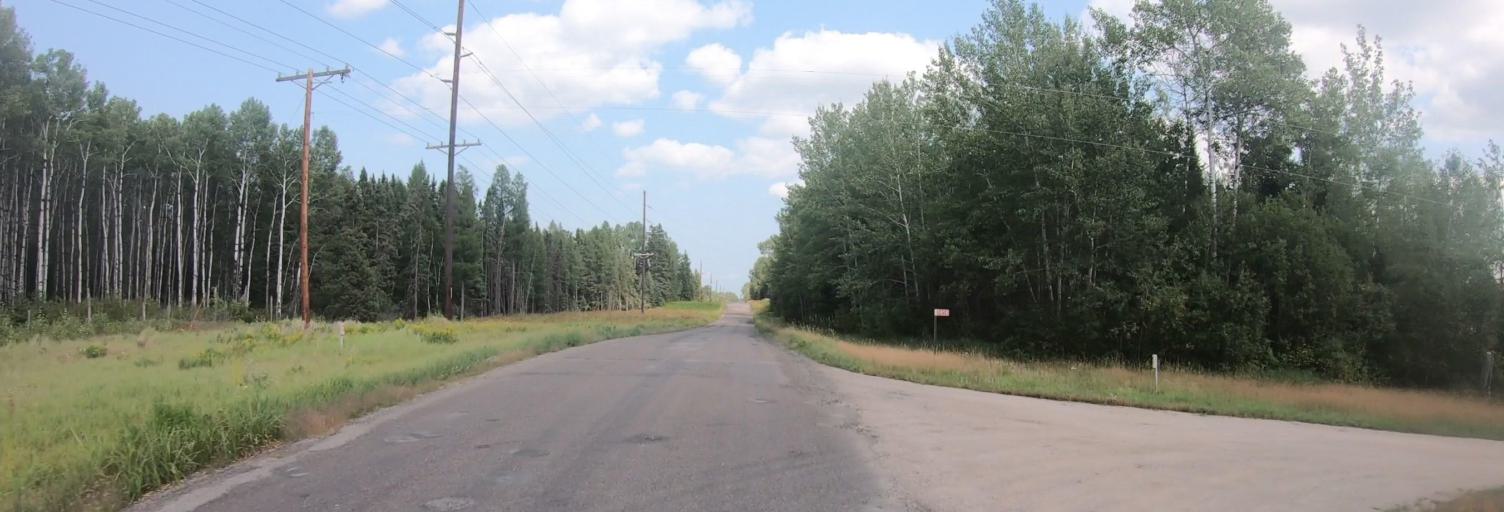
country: US
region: Minnesota
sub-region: Saint Louis County
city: Mountain Iron
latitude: 47.8921
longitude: -92.7333
